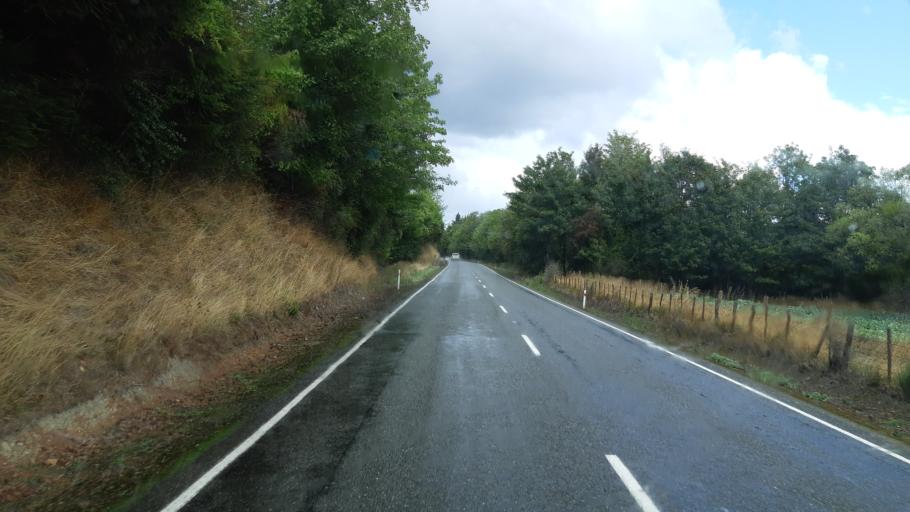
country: NZ
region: Tasman
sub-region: Tasman District
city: Wakefield
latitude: -41.4669
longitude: 172.8405
